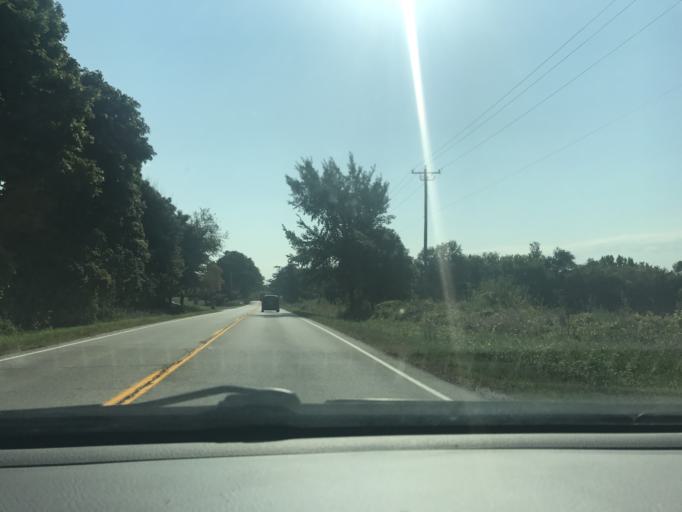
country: US
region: Illinois
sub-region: Kane County
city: Pingree Grove
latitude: 42.0458
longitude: -88.3849
